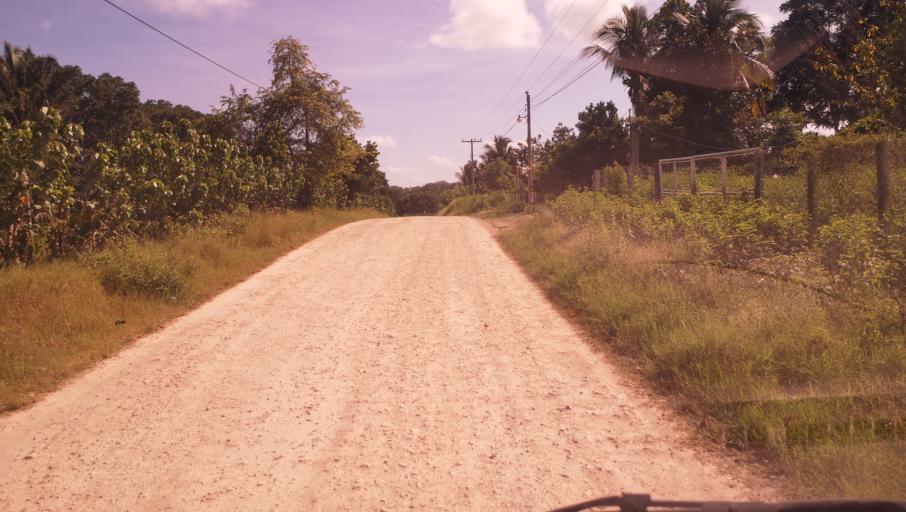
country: GT
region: Peten
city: Dolores
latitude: 16.7873
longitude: -89.3073
